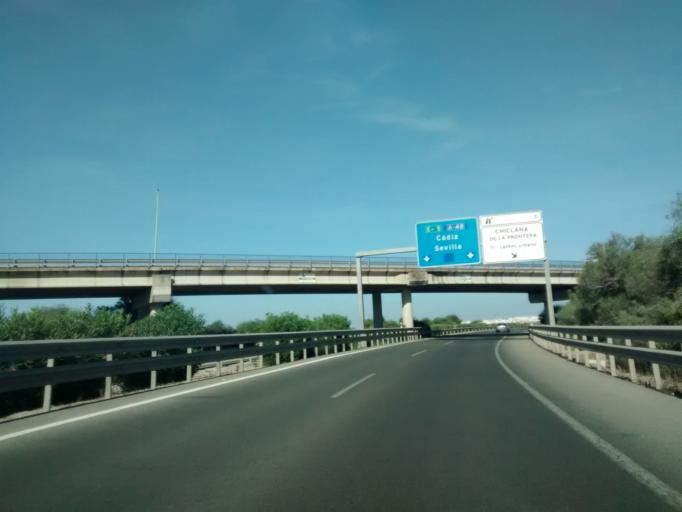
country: ES
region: Andalusia
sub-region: Provincia de Cadiz
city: Chiclana de la Frontera
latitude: 36.4447
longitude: -6.1443
